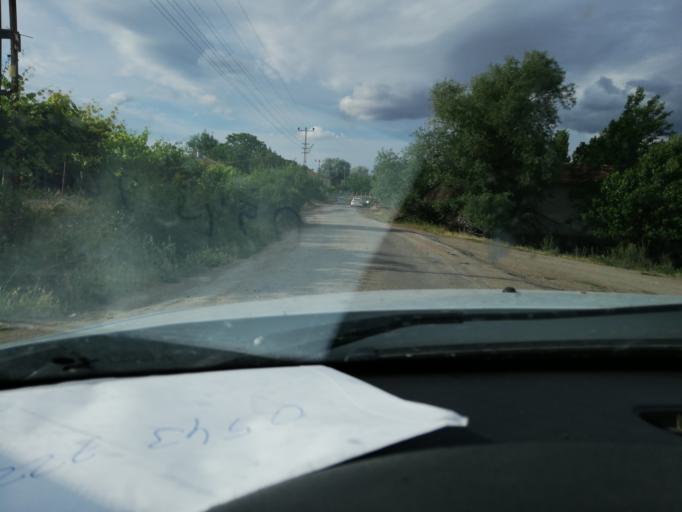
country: TR
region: Kirsehir
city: Kirsehir
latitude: 39.0245
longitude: 34.1248
